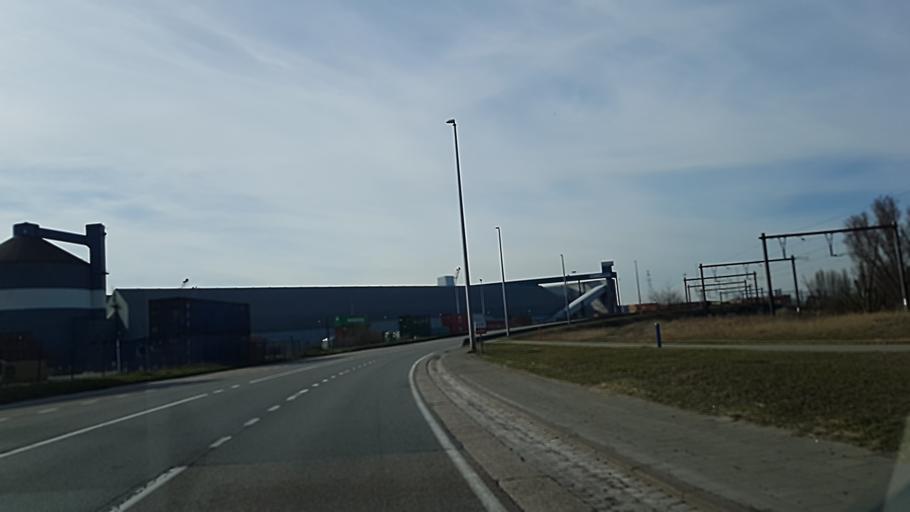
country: BE
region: Flanders
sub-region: Provincie Antwerpen
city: Stabroek
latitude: 51.2964
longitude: 4.3417
